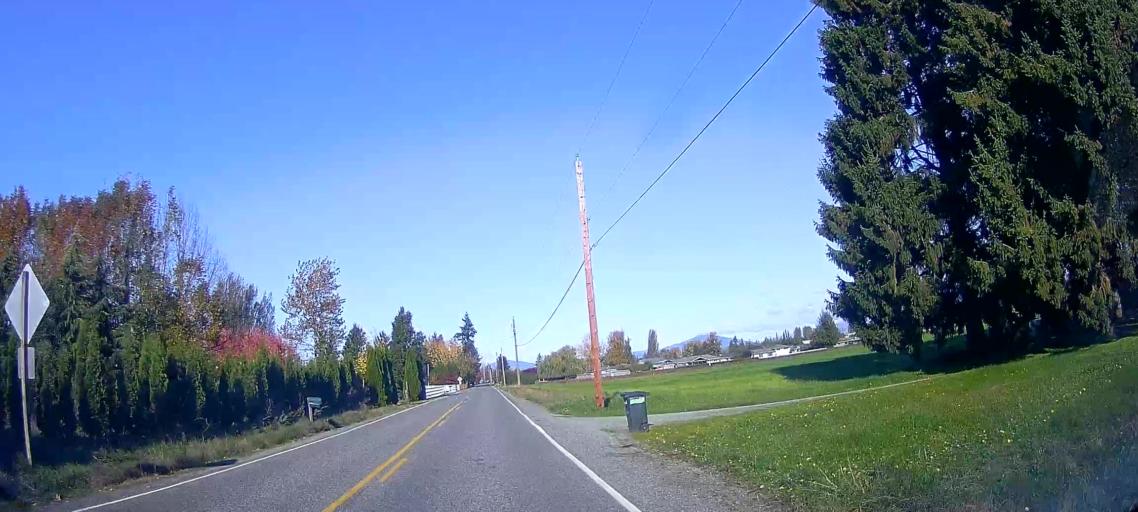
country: US
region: Washington
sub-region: Skagit County
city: Mount Vernon
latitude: 48.4154
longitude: -122.3652
